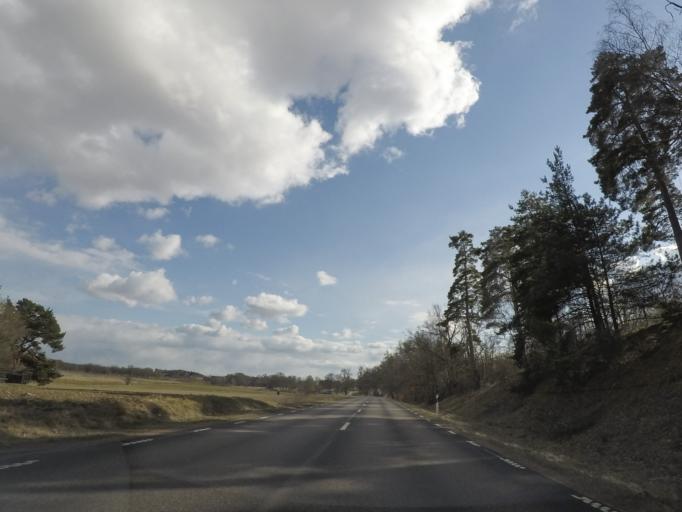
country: SE
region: Vaestmanland
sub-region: Hallstahammars Kommun
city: Kolback
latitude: 59.5333
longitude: 16.2476
